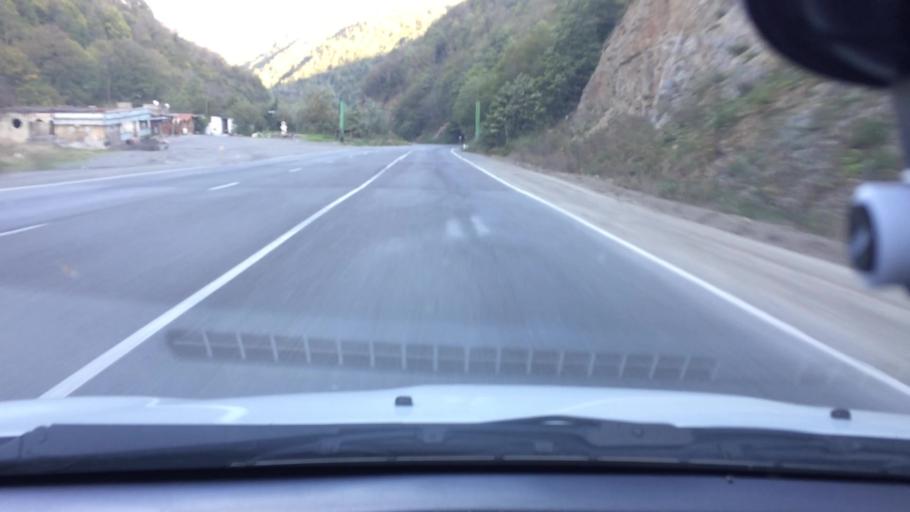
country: GE
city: Surami
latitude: 42.0867
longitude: 43.4670
